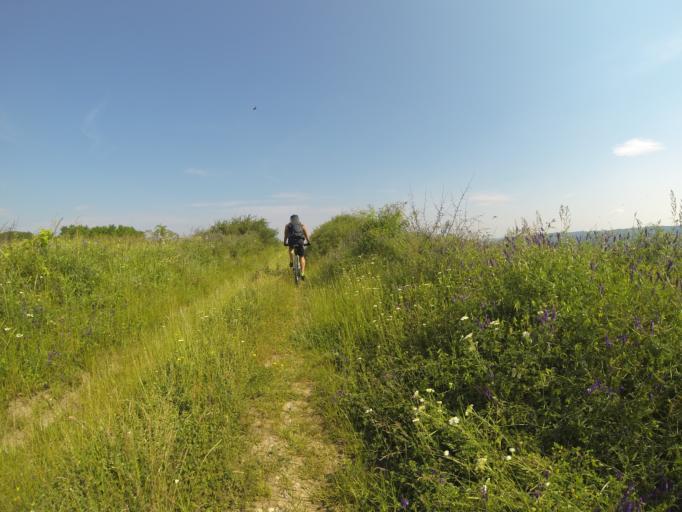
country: RO
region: Gorj
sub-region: Comuna Crusetu
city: Crusetu
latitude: 44.6088
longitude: 23.6696
